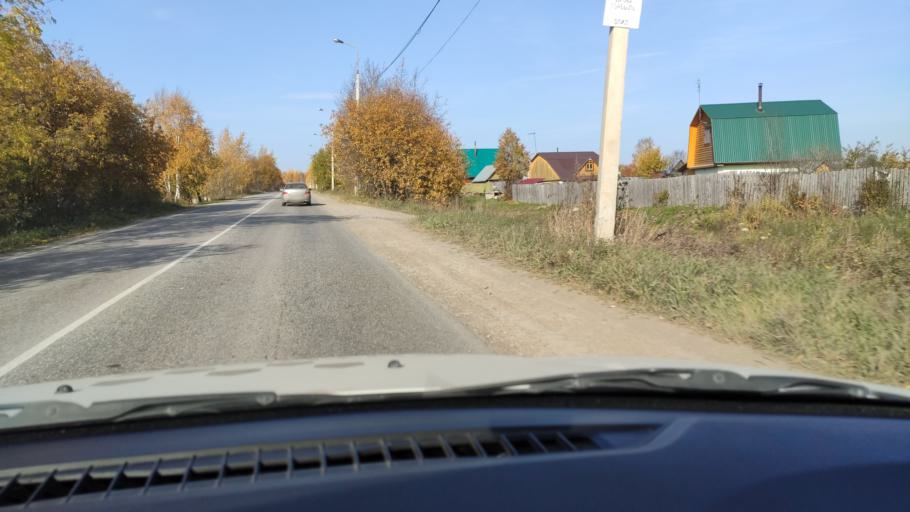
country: RU
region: Perm
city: Novyye Lyady
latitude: 58.0455
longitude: 56.5926
